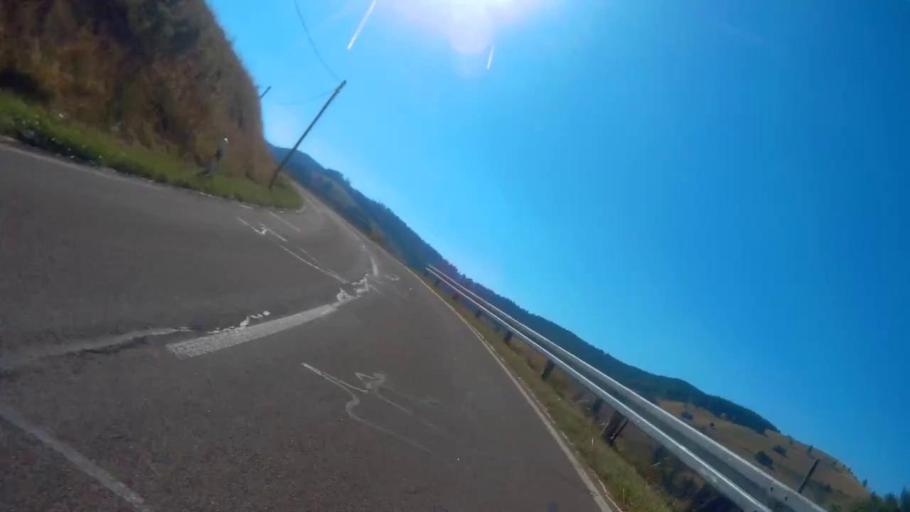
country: DE
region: Baden-Wuerttemberg
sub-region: Freiburg Region
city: Wembach
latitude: 47.7613
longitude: 7.9018
